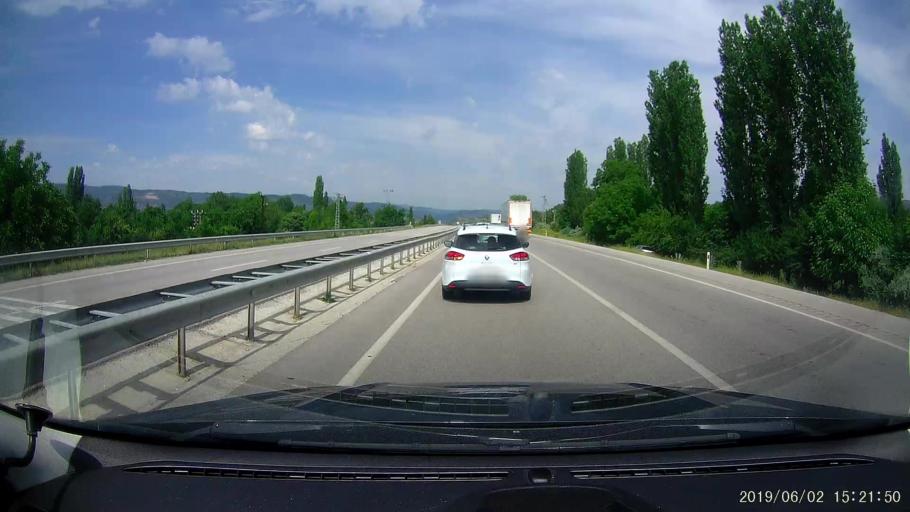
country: TR
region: Corum
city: Osmancik
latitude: 40.9789
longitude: 34.9449
